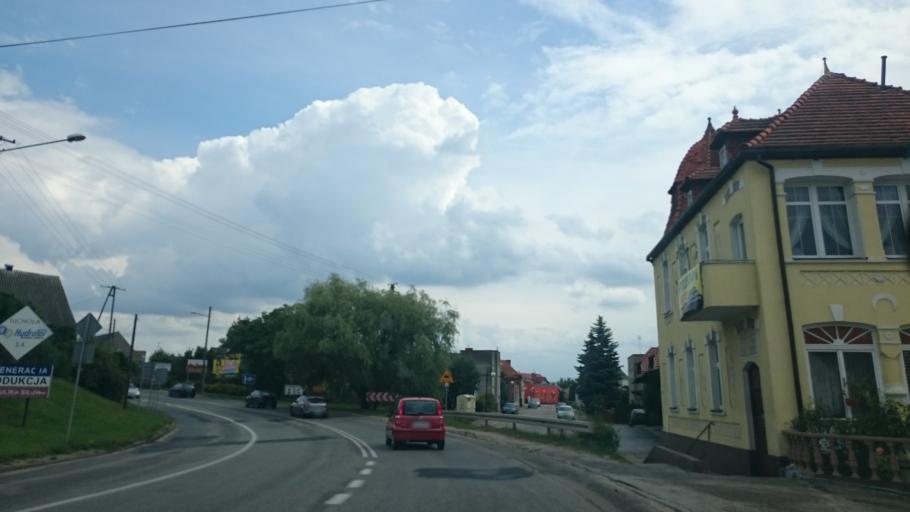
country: PL
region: Kujawsko-Pomorskie
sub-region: Powiat tucholski
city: Tuchola
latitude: 53.5933
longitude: 17.8555
